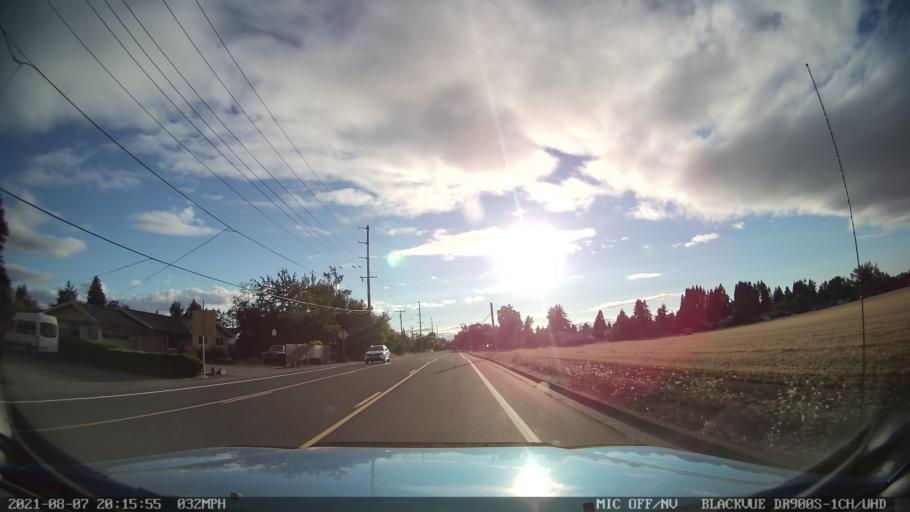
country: US
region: Oregon
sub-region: Marion County
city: Four Corners
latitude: 44.9549
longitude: -122.9601
